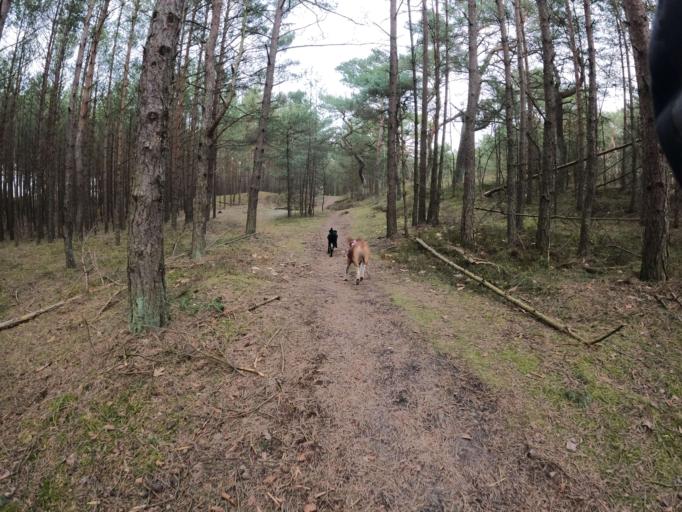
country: PL
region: West Pomeranian Voivodeship
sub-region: Powiat gryficki
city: Mrzezyno
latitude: 54.1329
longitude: 15.2432
